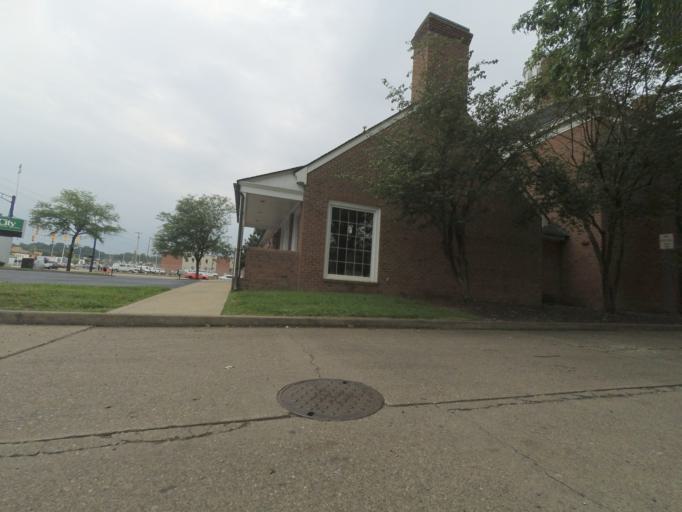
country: US
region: West Virginia
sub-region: Cabell County
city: Huntington
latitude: 38.4261
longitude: -82.4238
